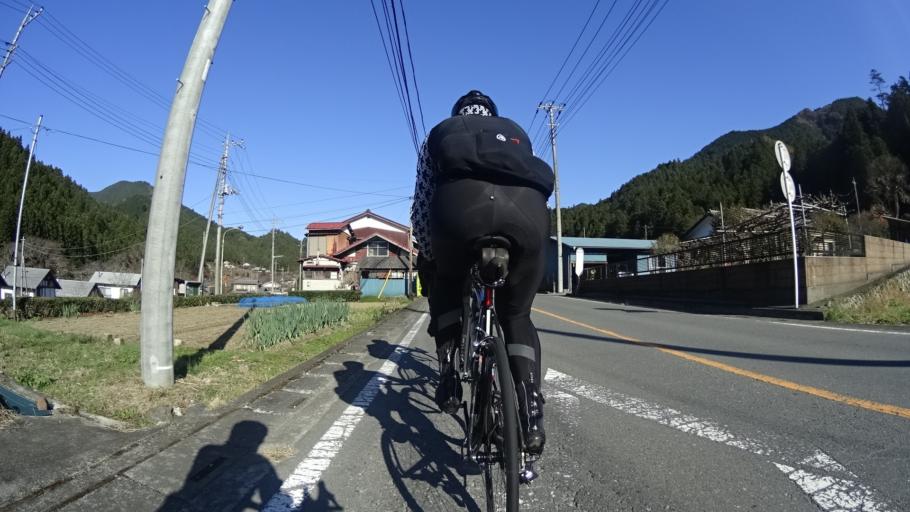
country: JP
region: Tokyo
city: Ome
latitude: 35.8676
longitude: 139.1869
